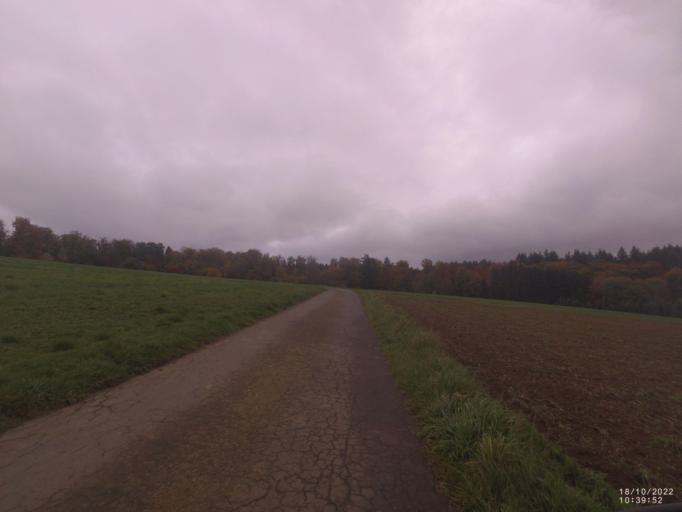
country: DE
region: Rheinland-Pfalz
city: Darscheid
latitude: 50.2222
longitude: 6.9010
